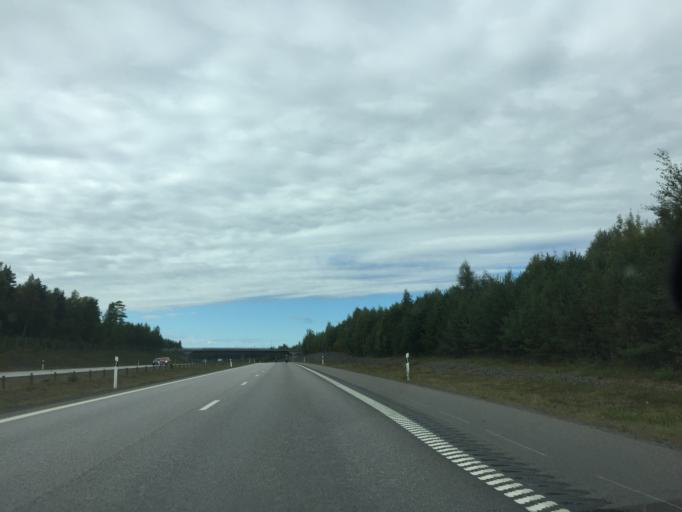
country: SE
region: Vaestmanland
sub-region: Arboga Kommun
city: Arboga
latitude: 59.4012
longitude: 15.7284
